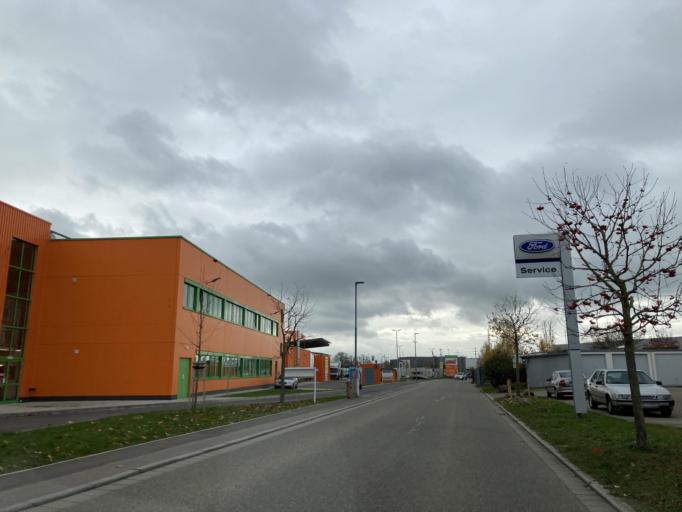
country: DE
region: Baden-Wuerttemberg
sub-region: Freiburg Region
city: Auggen
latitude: 47.8065
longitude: 7.6033
